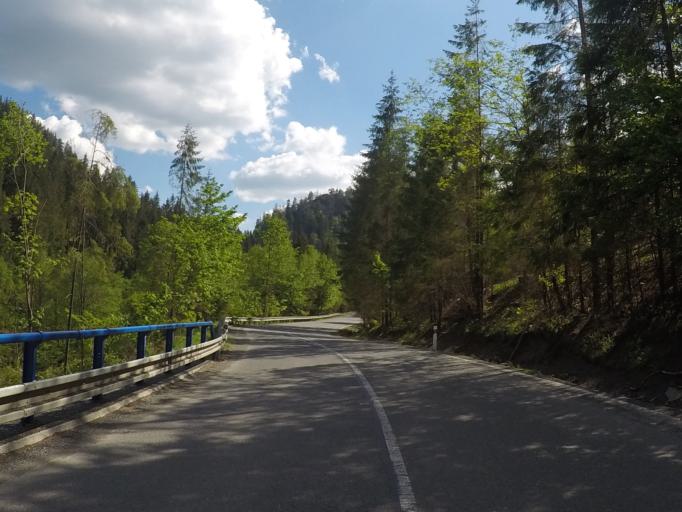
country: SK
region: Presovsky
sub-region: Okres Poprad
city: Poprad
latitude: 48.9387
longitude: 20.2865
